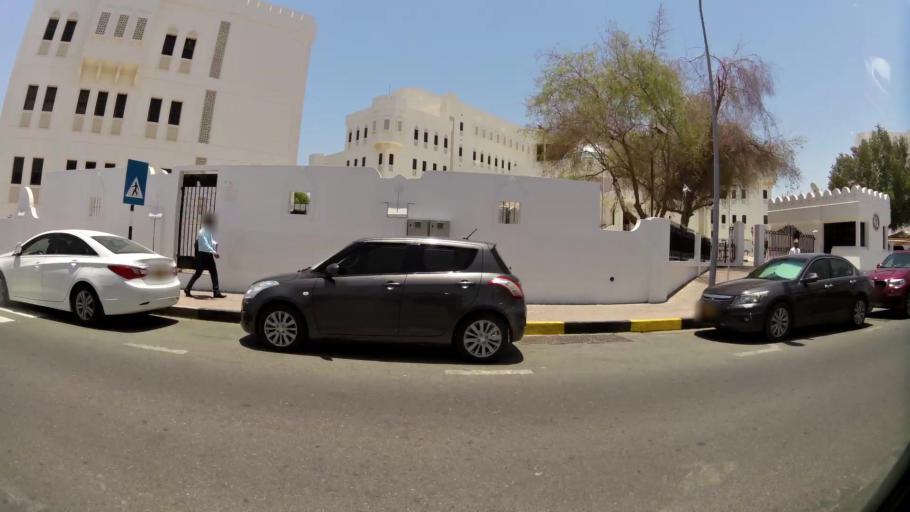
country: OM
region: Muhafazat Masqat
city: Muscat
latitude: 23.6152
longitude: 58.5424
